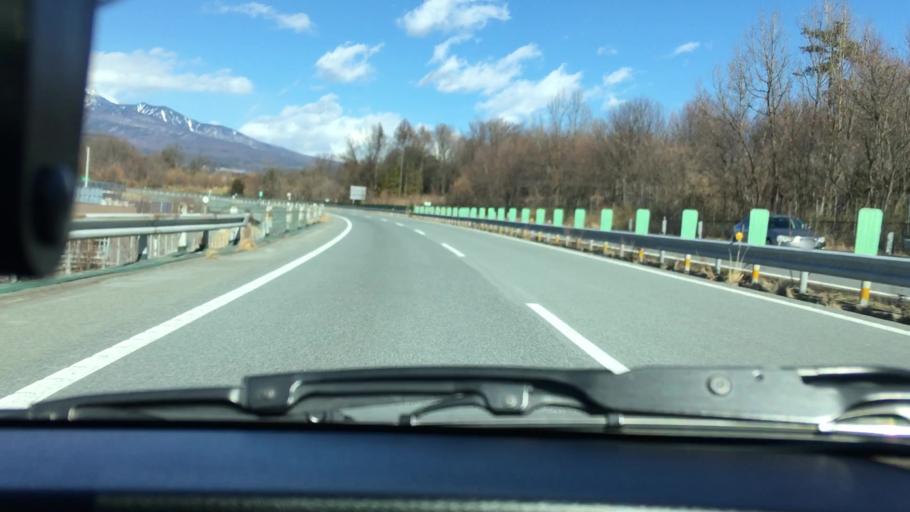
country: JP
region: Yamanashi
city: Nirasaki
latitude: 35.8204
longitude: 138.3944
